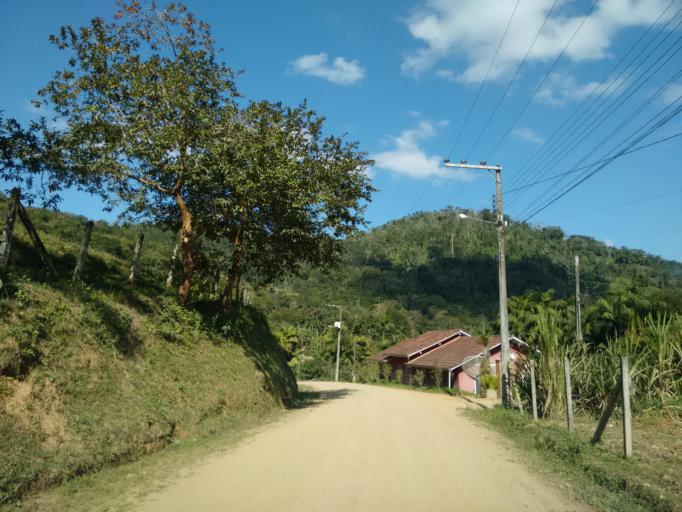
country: BR
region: Santa Catarina
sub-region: Pomerode
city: Pomerode
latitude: -26.7412
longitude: -49.1575
